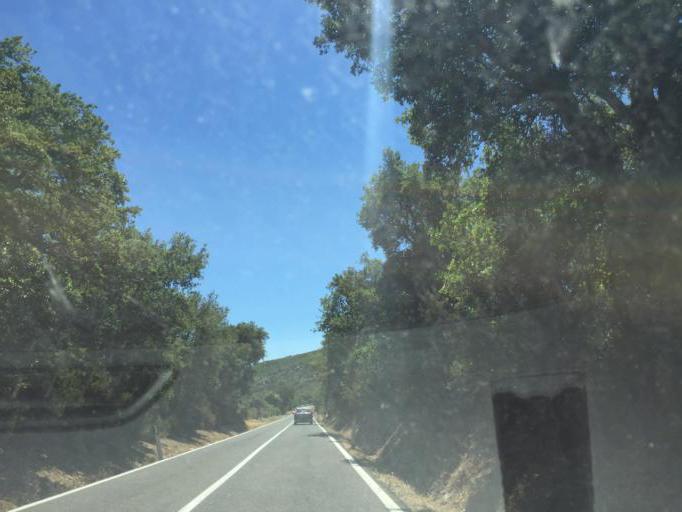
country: IT
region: Sardinia
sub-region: Provincia di Olbia-Tempio
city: Calangianus
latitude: 40.8925
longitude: 9.2421
